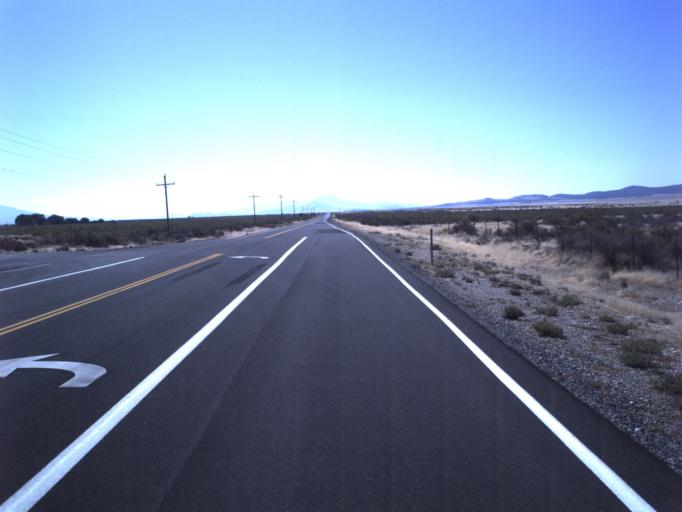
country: US
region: Utah
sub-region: Tooele County
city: Grantsville
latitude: 40.3545
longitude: -112.7456
